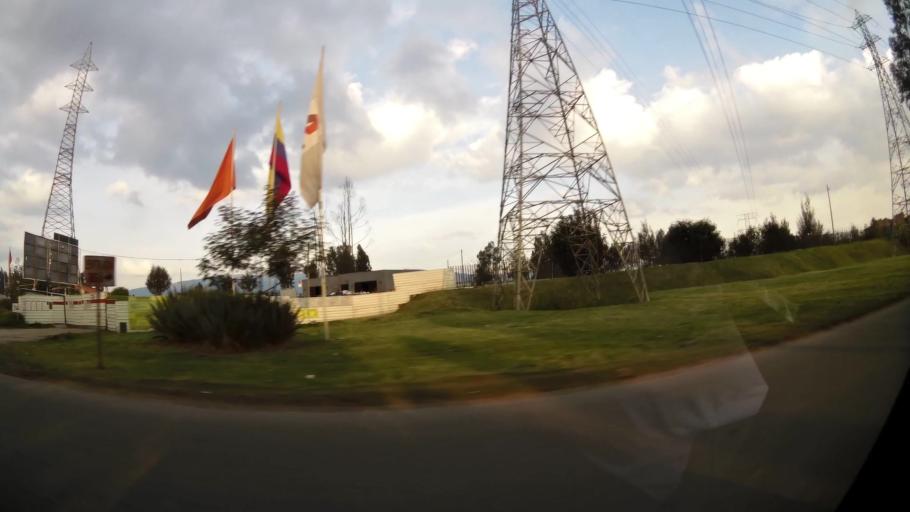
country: CO
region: Cundinamarca
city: Cota
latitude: 4.8113
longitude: -74.0912
